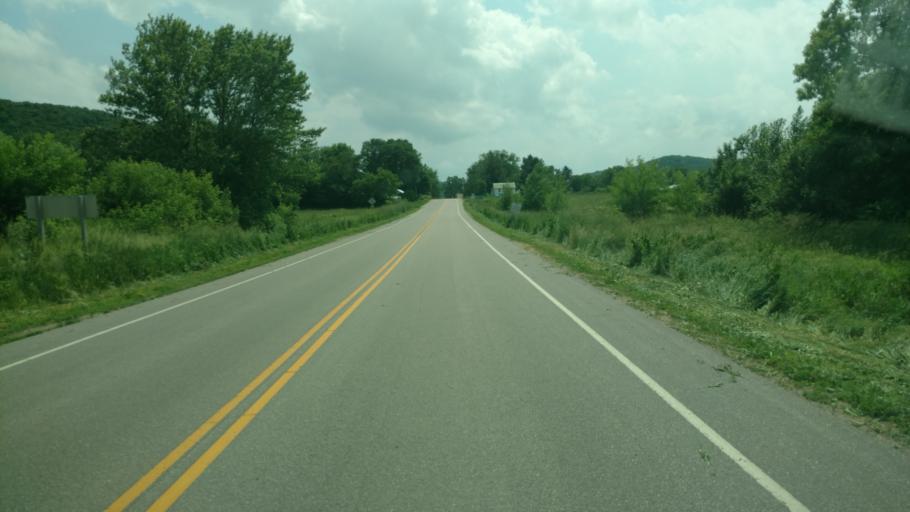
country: US
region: Wisconsin
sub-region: Vernon County
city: Viroqua
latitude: 43.4553
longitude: -90.7581
